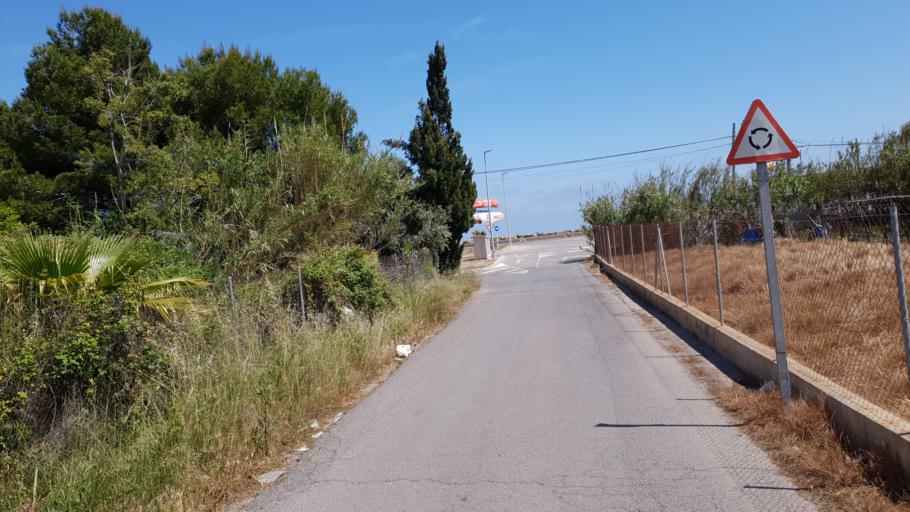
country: ES
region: Valencia
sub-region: Provincia de Castello
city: Burriana
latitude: 39.8580
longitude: -0.0864
